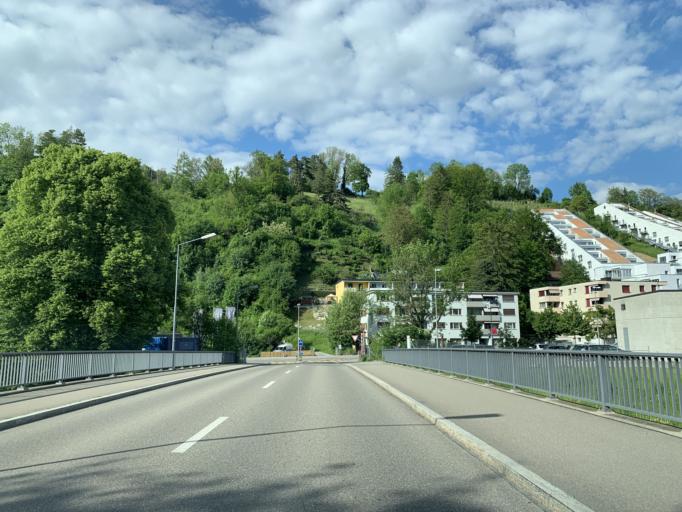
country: CH
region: Zurich
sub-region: Bezirk Winterthur
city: Wuelflingen (Kreis 6) / Oberfeld
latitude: 47.4963
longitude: 8.7002
